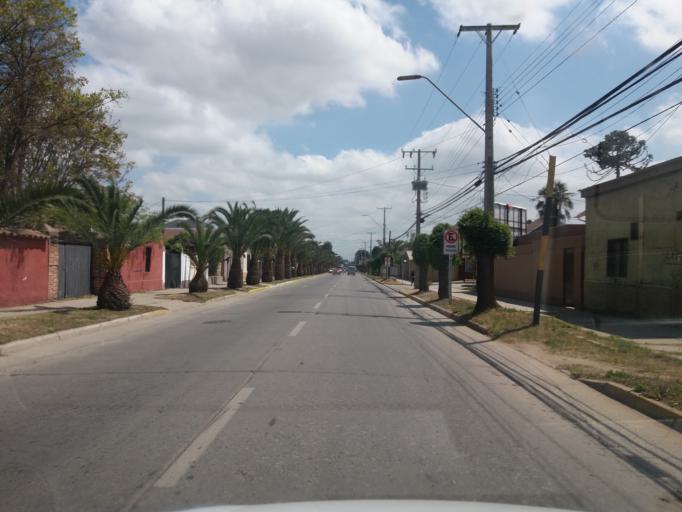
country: CL
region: Valparaiso
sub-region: Provincia de Marga Marga
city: Limache
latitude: -33.0072
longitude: -71.2532
